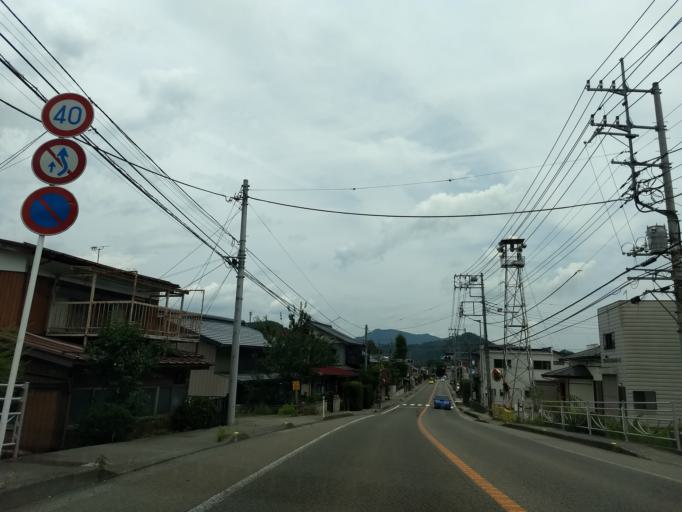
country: JP
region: Yamanashi
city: Otsuki
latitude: 35.5393
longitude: 138.8862
